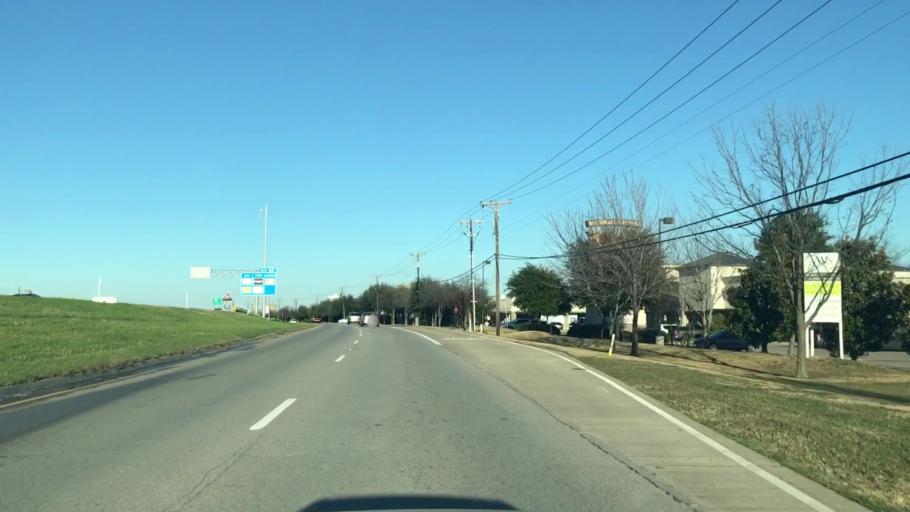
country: US
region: Texas
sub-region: Rockwall County
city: Rockwall
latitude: 32.9012
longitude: -96.4570
